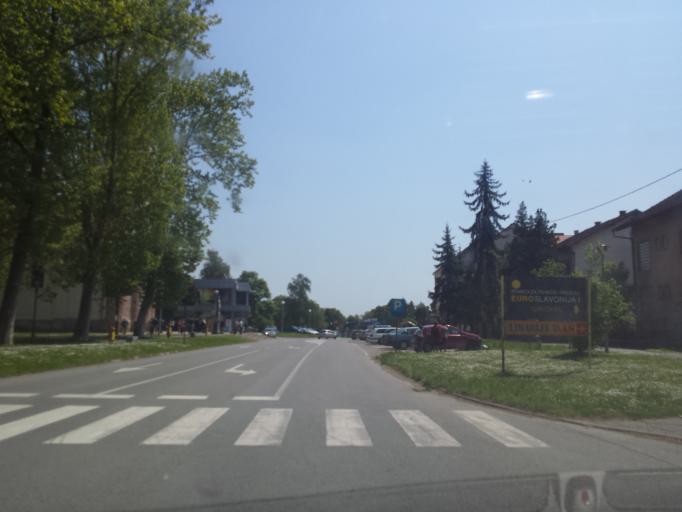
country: HR
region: Brodsko-Posavska
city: Oriovac
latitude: 45.1662
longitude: 17.7536
